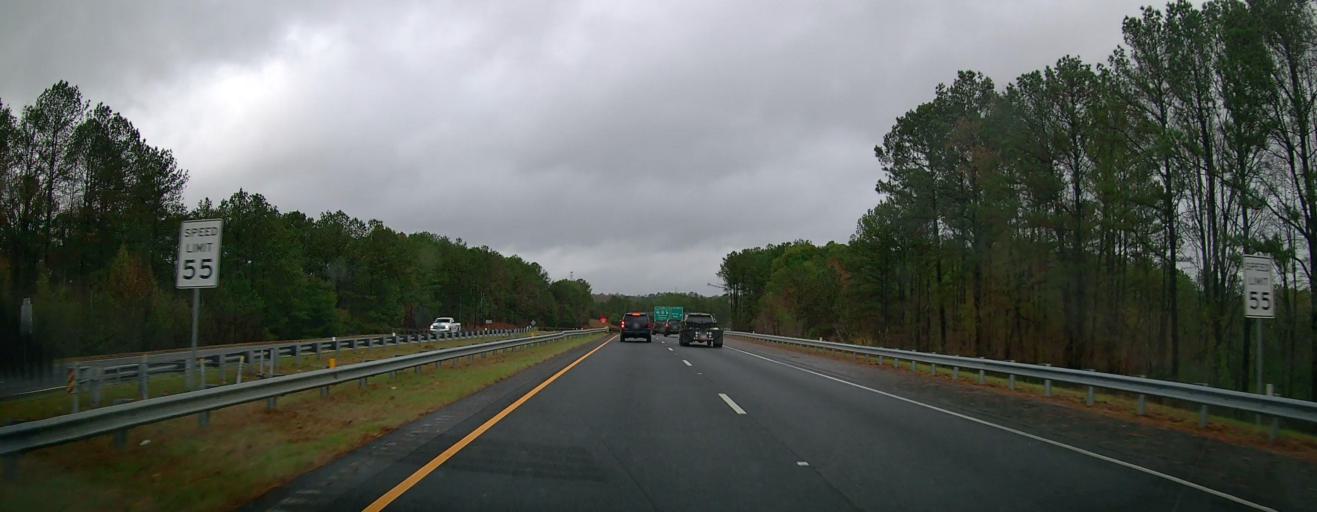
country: US
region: Georgia
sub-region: Clarke County
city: Athens
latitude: 33.9704
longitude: -83.3545
